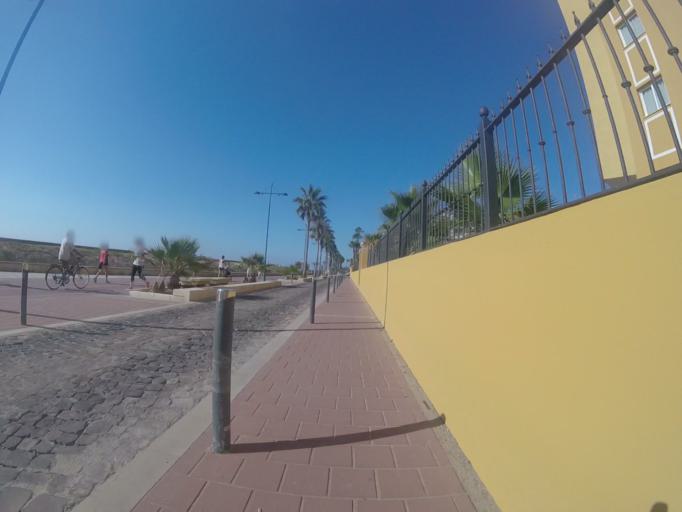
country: ES
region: Valencia
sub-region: Provincia de Castello
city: Benicarlo
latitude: 40.3926
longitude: 0.4133
